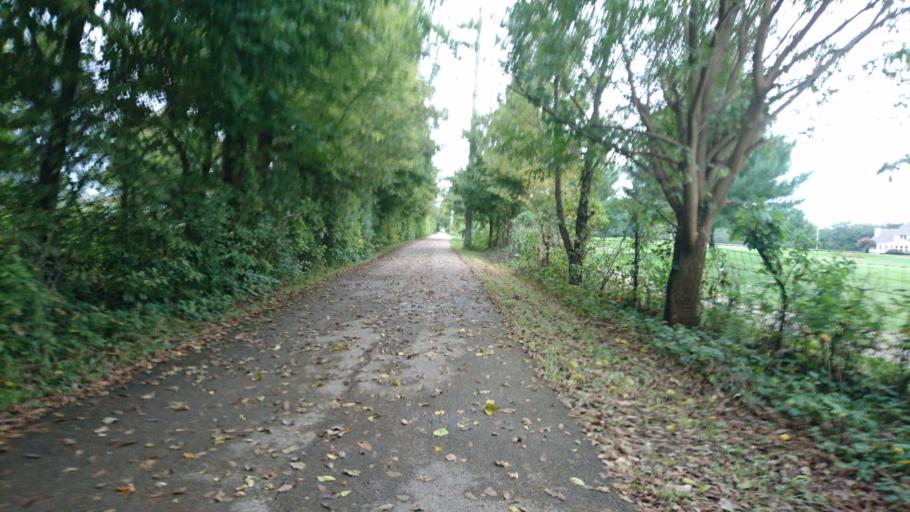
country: US
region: Illinois
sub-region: Sangamon County
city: Chatham
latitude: 39.6905
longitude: -89.6959
